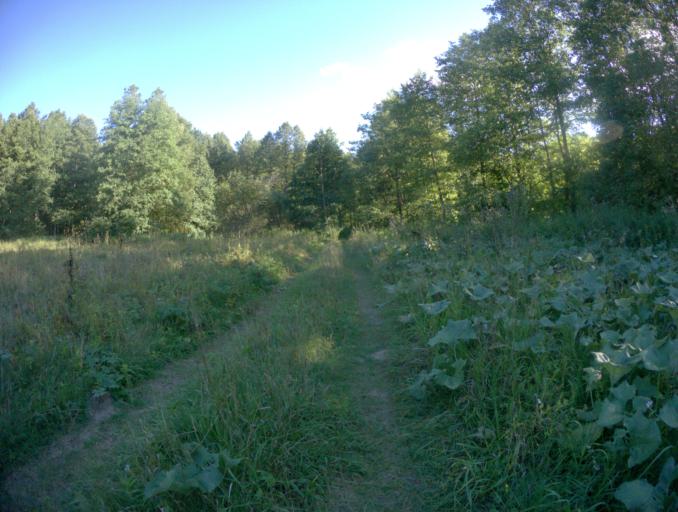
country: RU
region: Vladimir
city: Krasnaya Gorbatka
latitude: 55.7888
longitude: 41.6620
